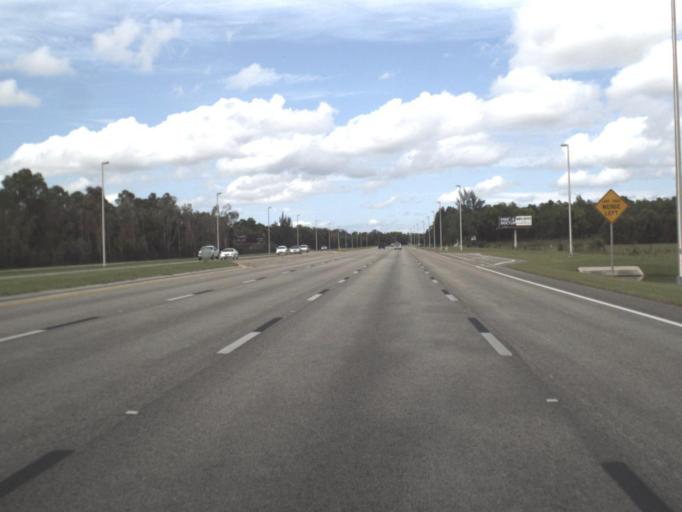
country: US
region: Florida
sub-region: Lee County
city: Villas
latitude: 26.5030
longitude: -81.8476
